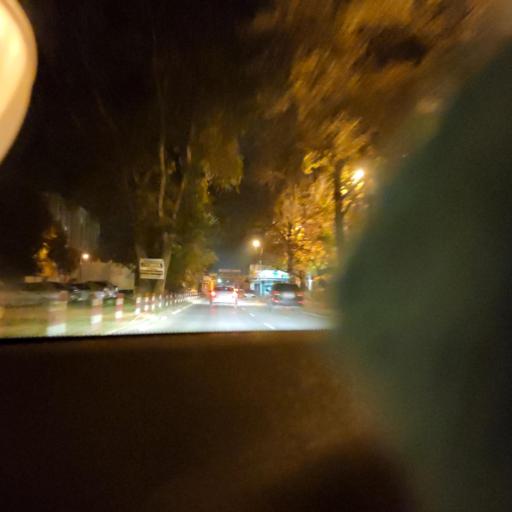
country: RU
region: Samara
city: Samara
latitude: 53.2107
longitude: 50.2509
